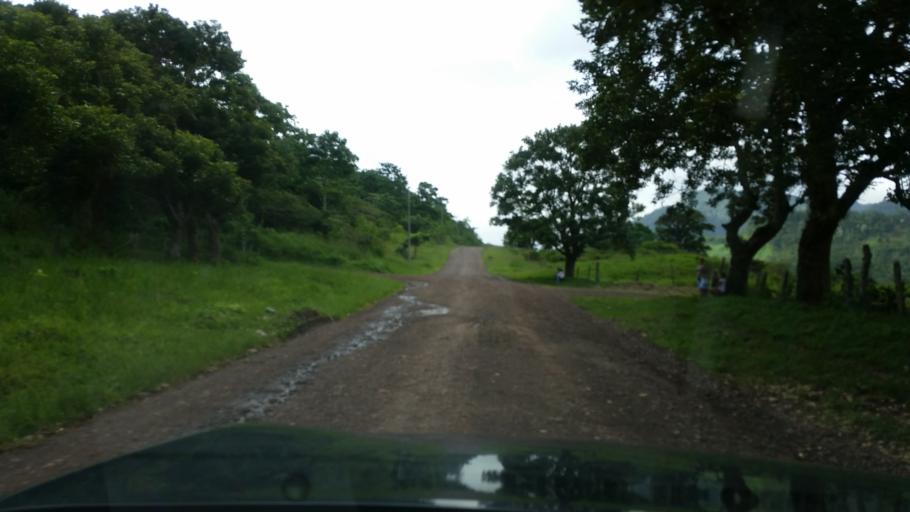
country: NI
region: Jinotega
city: Jinotega
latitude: 13.2242
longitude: -85.7304
